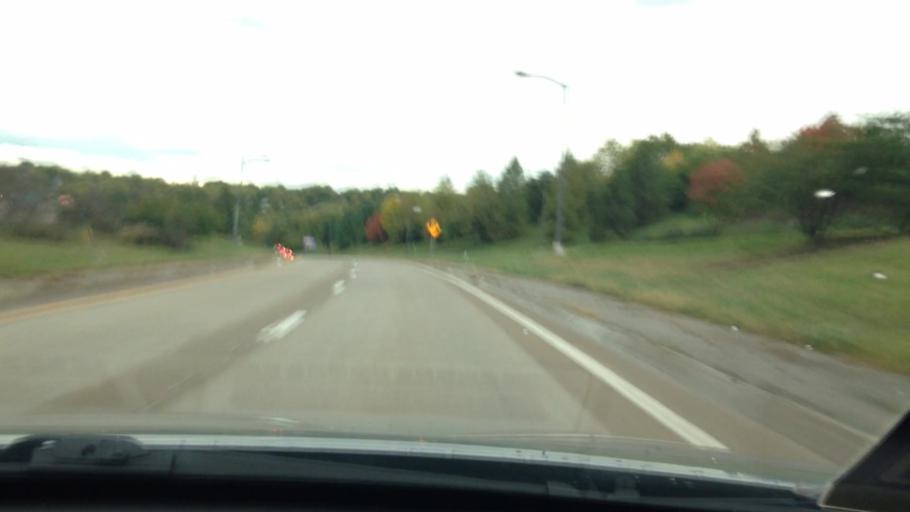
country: US
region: Missouri
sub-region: Jackson County
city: Kansas City
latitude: 39.0474
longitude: -94.5622
